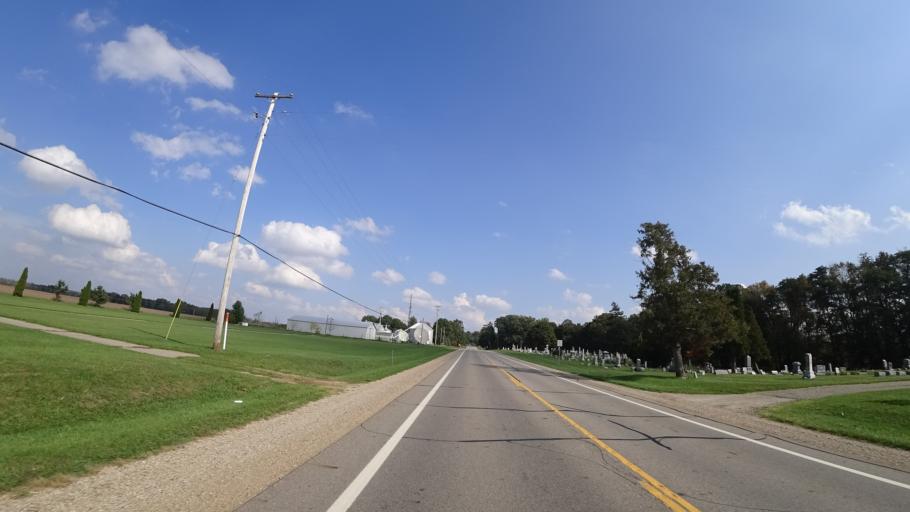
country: US
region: Michigan
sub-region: Saint Joseph County
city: Centreville
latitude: 42.0063
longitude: -85.4794
